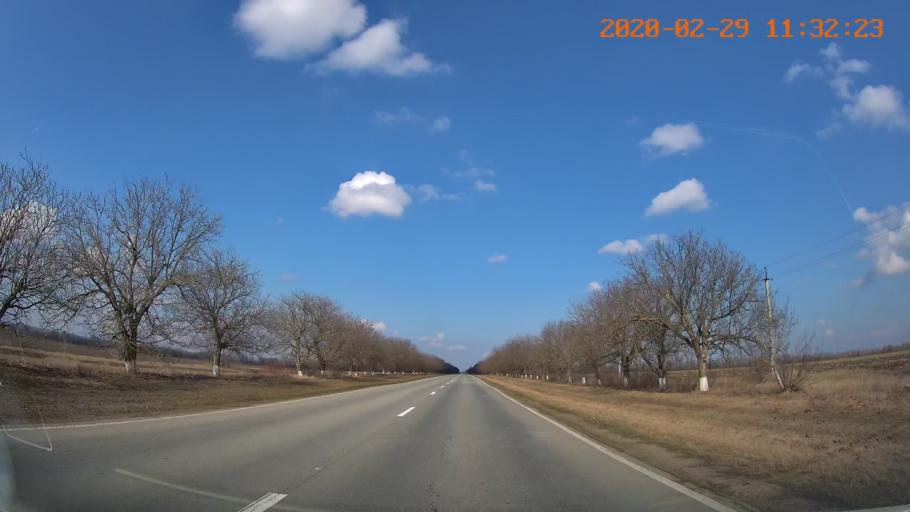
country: MD
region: Rezina
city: Saharna
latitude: 47.5372
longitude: 29.0950
